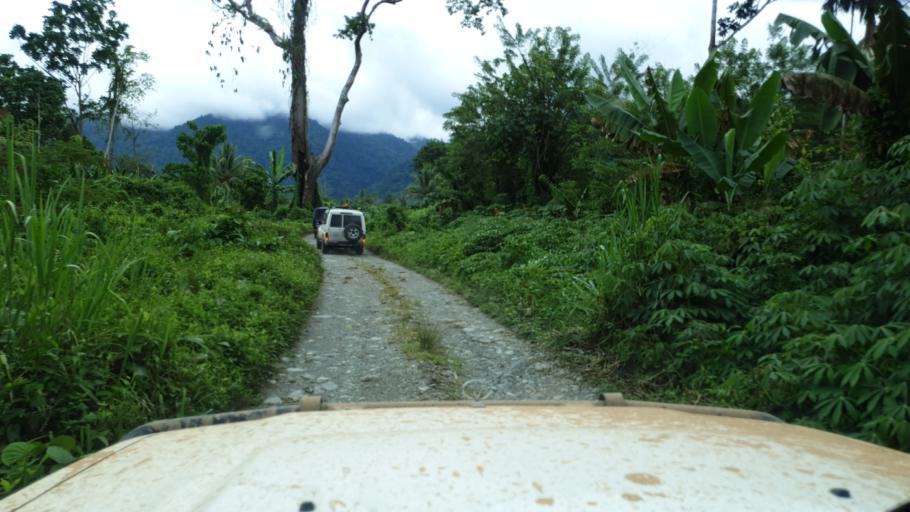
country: PG
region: Northern Province
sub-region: Sohe
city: Kokoda
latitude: -8.9379
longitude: 147.8675
